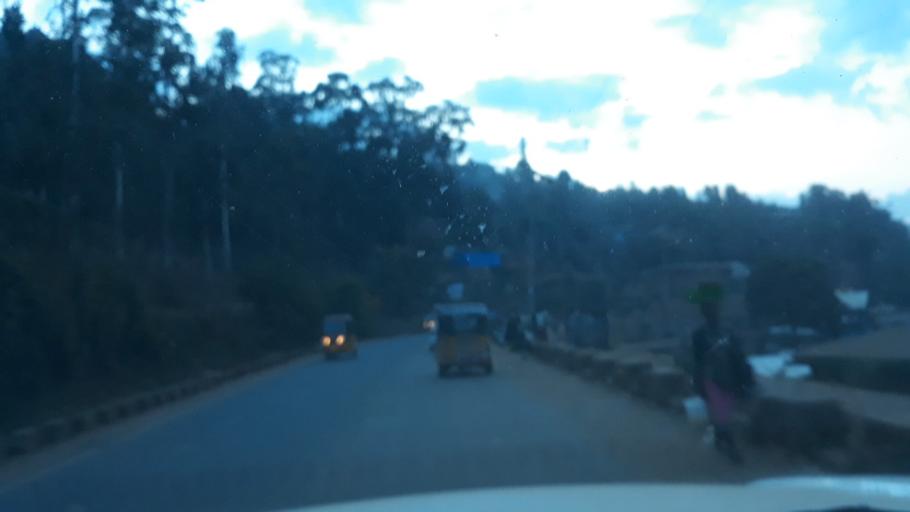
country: CD
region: South Kivu
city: Bukavu
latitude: -2.5390
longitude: 28.8600
